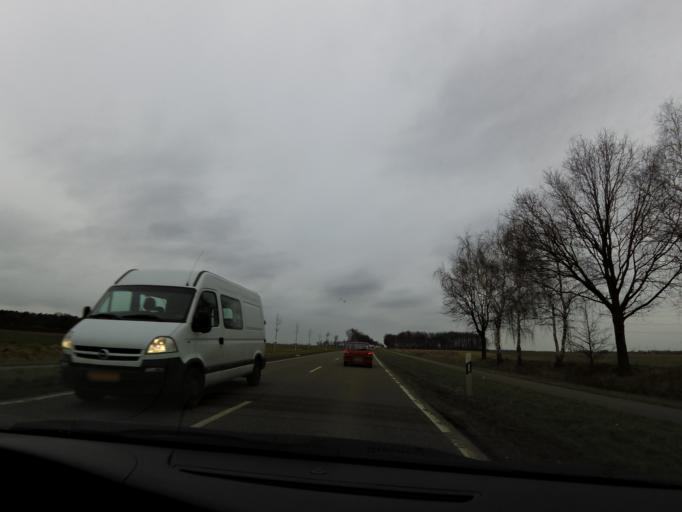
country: DE
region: North Rhine-Westphalia
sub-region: Regierungsbezirk Koln
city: Selfkant
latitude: 51.0037
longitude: 5.9514
